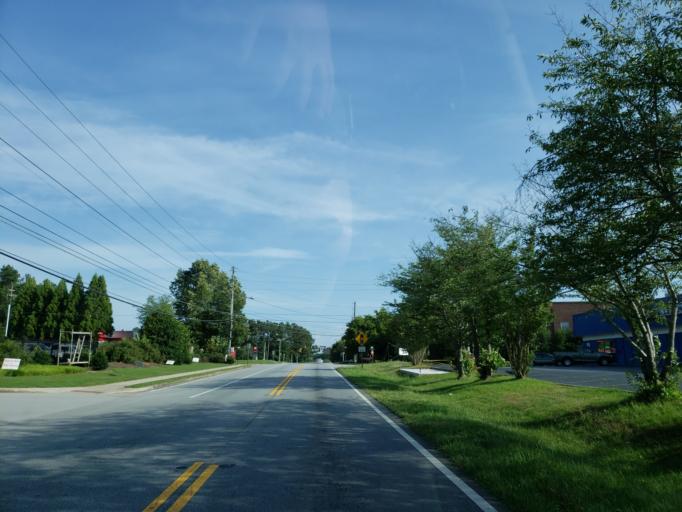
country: US
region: Georgia
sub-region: Cobb County
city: Powder Springs
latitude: 33.8769
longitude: -84.7036
